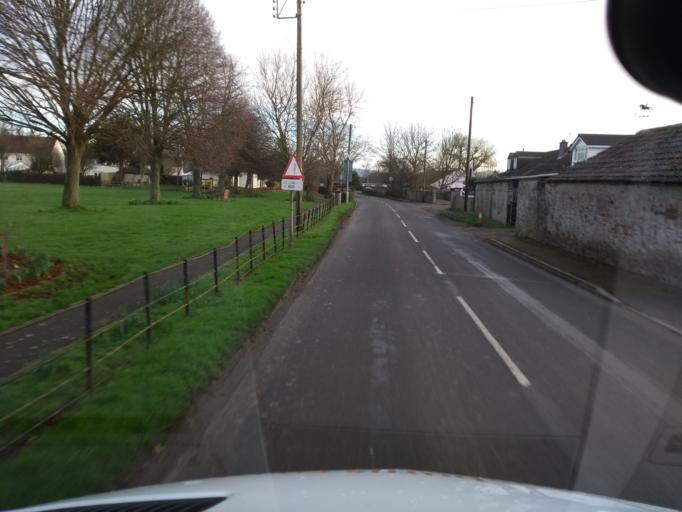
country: GB
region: England
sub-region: North Somerset
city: Bleadon
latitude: 51.2843
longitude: -2.9529
